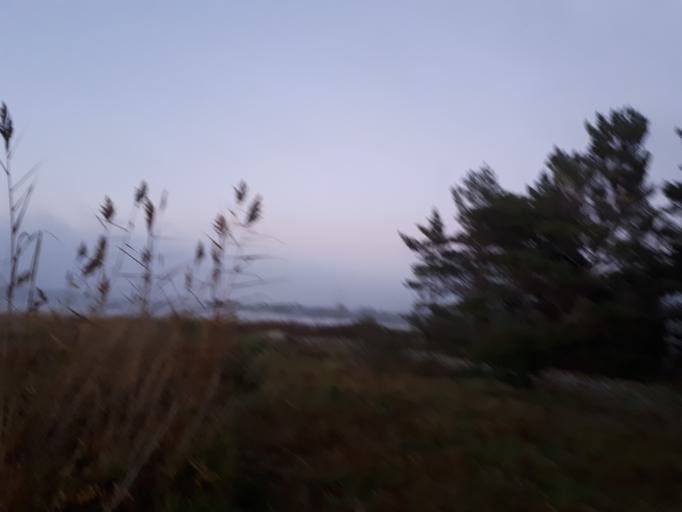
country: SE
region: Gotland
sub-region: Gotland
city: Visby
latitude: 57.6887
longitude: 18.3475
